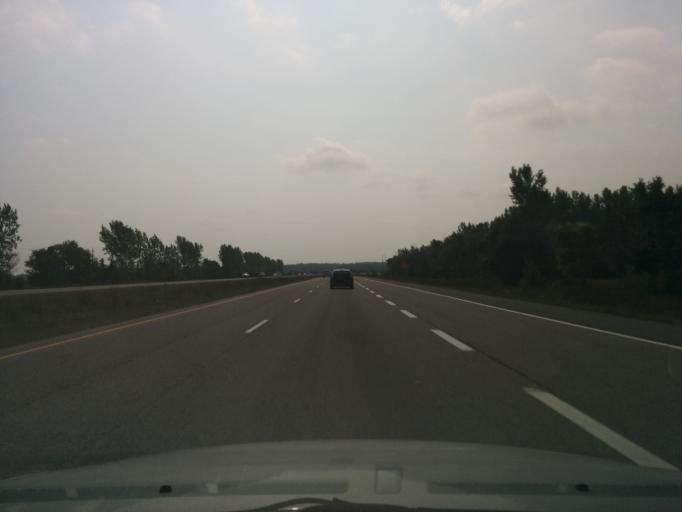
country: CA
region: Ontario
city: Bells Corners
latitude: 45.3076
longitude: -75.7975
